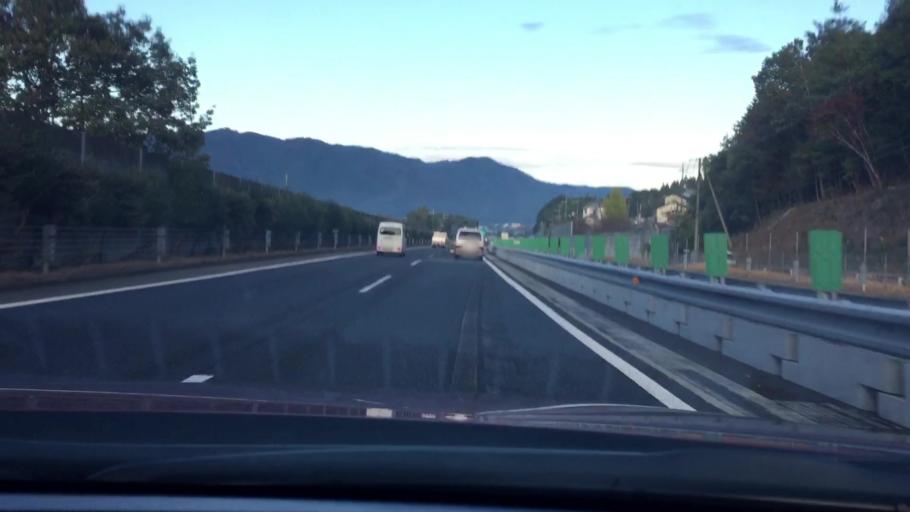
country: JP
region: Hyogo
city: Yamazakicho-nakabirose
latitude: 34.9952
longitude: 134.5660
